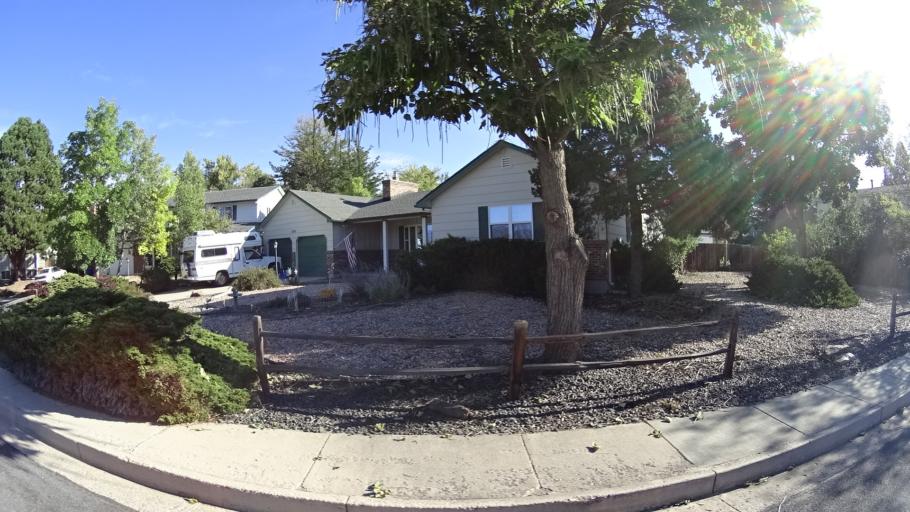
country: US
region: Colorado
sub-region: El Paso County
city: Cimarron Hills
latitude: 38.9107
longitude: -104.7659
